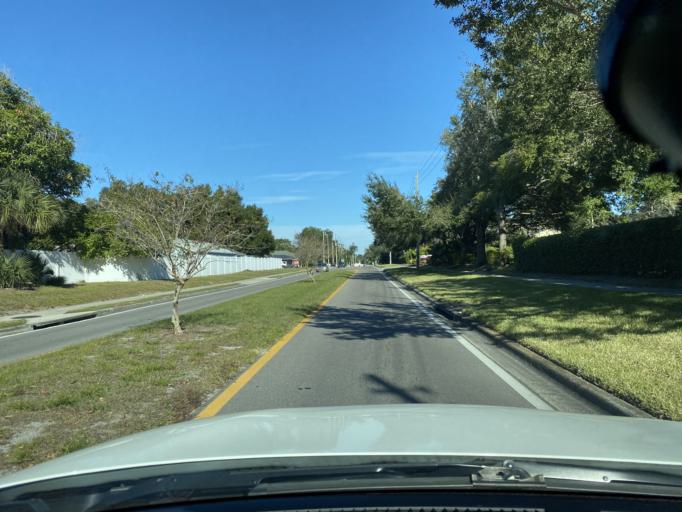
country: US
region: Florida
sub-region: Orange County
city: Conway
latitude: 28.5198
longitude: -81.3145
